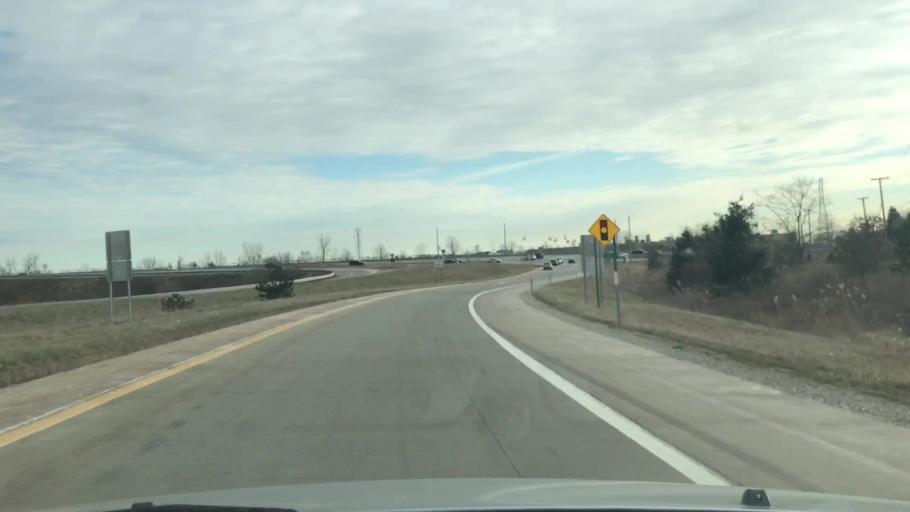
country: US
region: Michigan
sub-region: Oakland County
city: Rochester Hills
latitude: 42.6444
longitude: -83.1970
